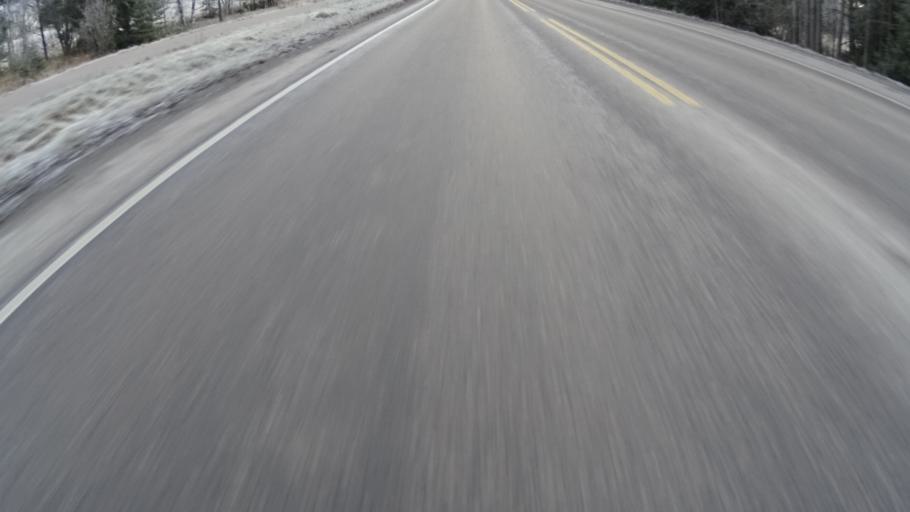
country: FI
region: Uusimaa
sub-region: Helsinki
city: Nurmijaervi
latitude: 60.3593
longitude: 24.7931
